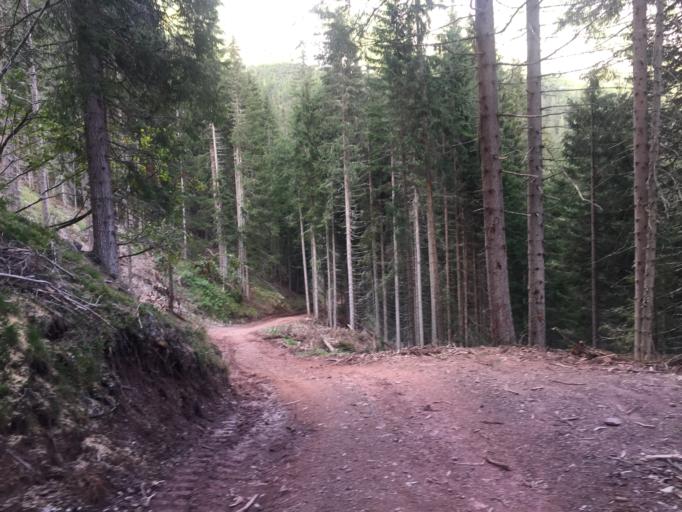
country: IT
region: Veneto
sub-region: Provincia di Belluno
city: San Pietro di Cadore
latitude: 46.6081
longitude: 12.5679
